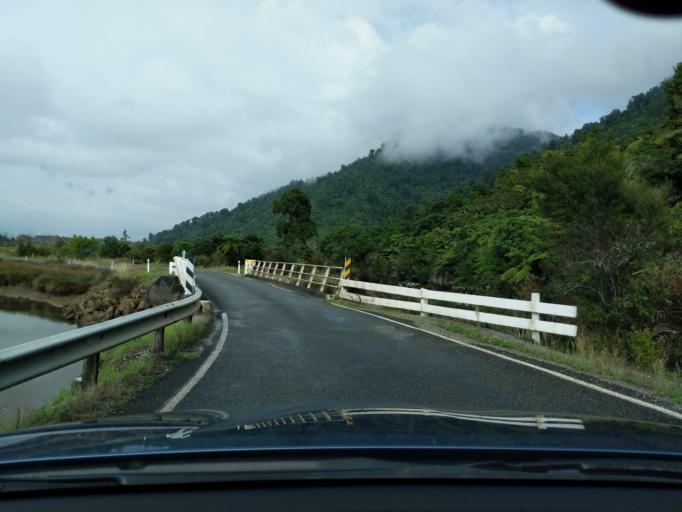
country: NZ
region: Tasman
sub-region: Tasman District
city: Takaka
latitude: -40.6558
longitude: 172.6465
